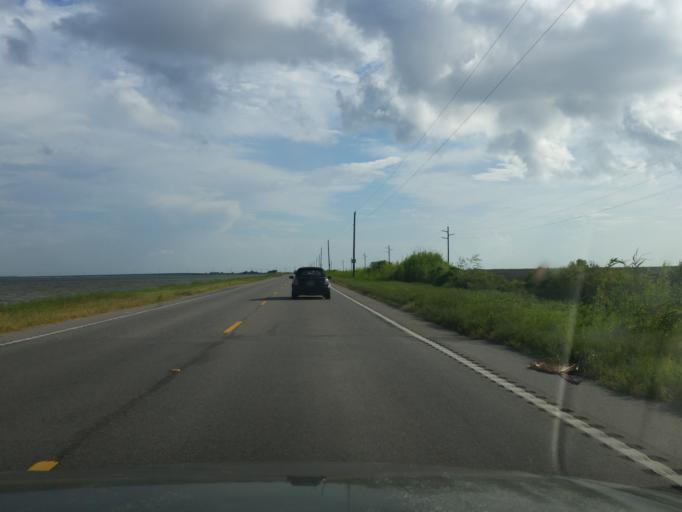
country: US
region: Alabama
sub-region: Mobile County
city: Dauphin Island
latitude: 30.3315
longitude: -88.1331
